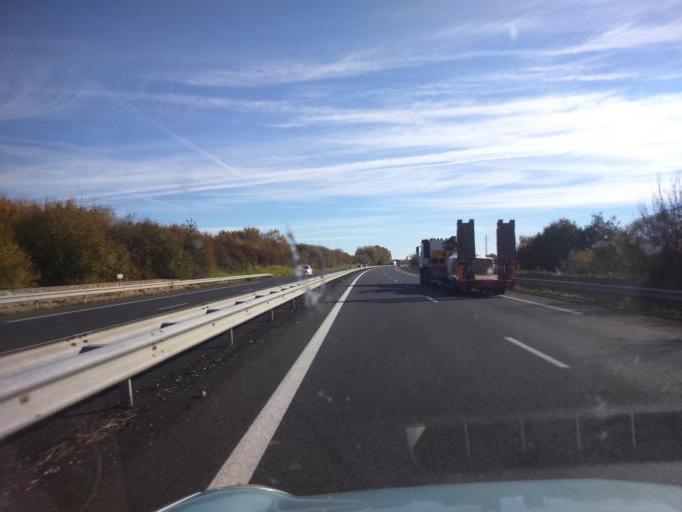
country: FR
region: Poitou-Charentes
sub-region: Departement de la Charente-Maritime
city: Tonnay-Charente
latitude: 45.9573
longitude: -0.9183
